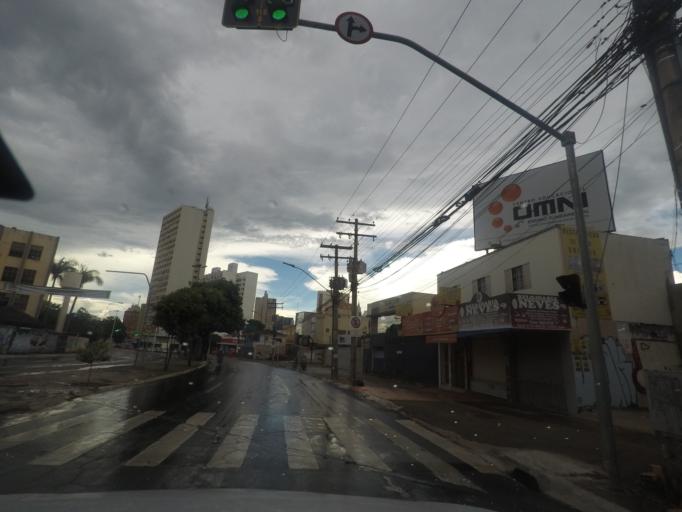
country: BR
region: Goias
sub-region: Goiania
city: Goiania
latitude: -16.6814
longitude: -49.2546
